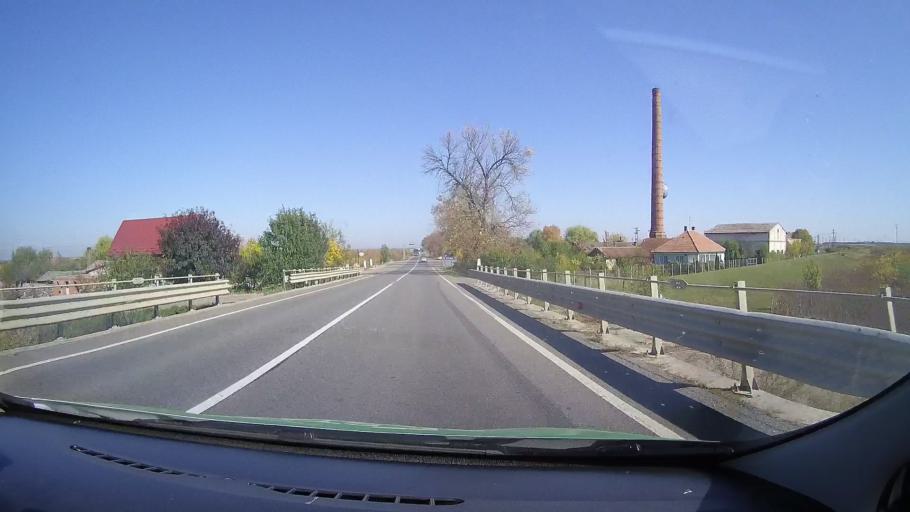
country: RO
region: Satu Mare
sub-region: Comuna Moftinu
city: Moftinu Mic
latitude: 47.7071
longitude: 22.6374
